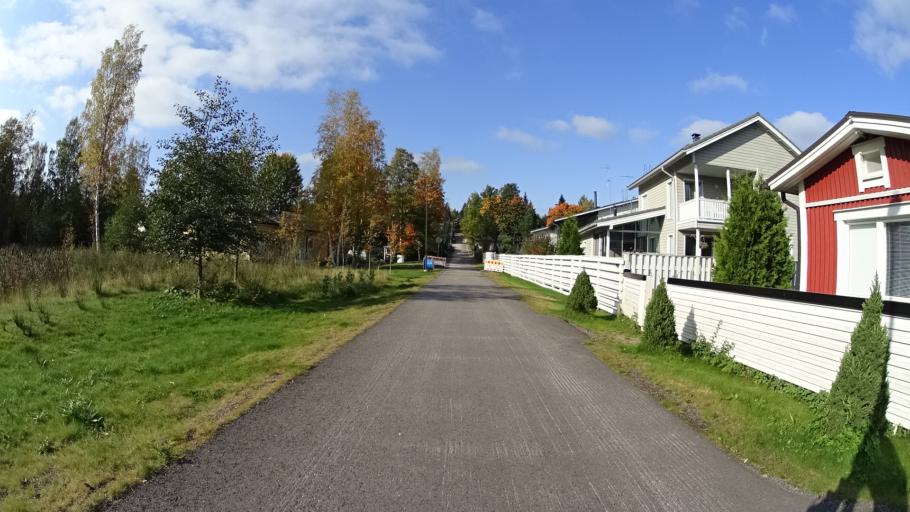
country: FI
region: Uusimaa
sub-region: Helsinki
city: Kilo
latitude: 60.2343
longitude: 24.8052
